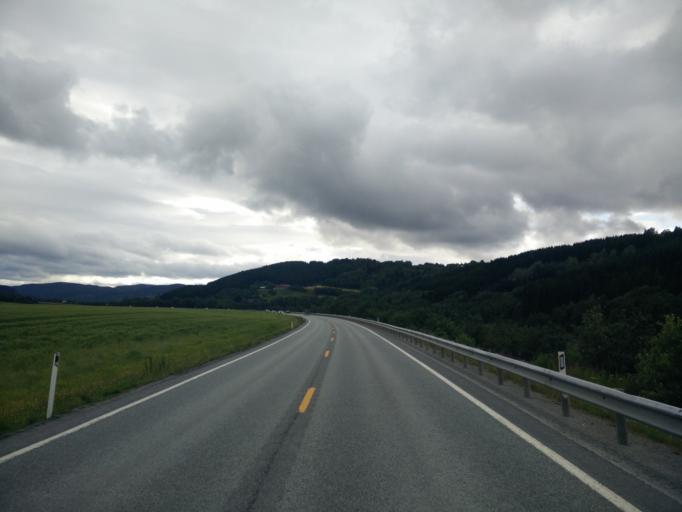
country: NO
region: Sor-Trondelag
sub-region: Orkdal
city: Orkanger
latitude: 63.2763
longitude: 9.8124
